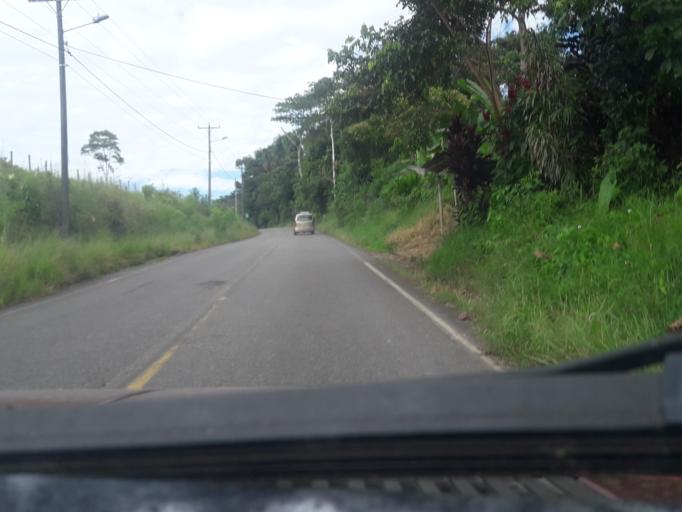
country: EC
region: Napo
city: Tena
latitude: -1.0344
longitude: -77.8898
